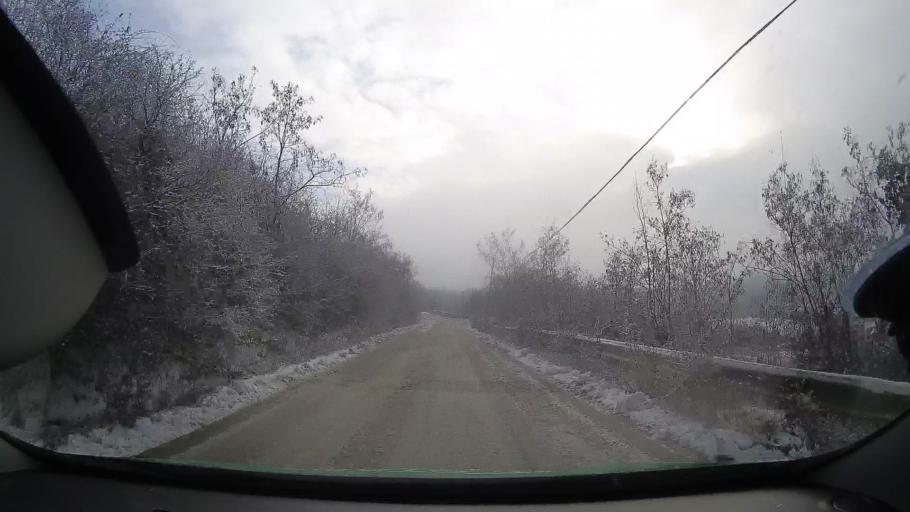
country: RO
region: Mures
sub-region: Comuna Chetani
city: Chetani
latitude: 46.4268
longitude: 24.0102
